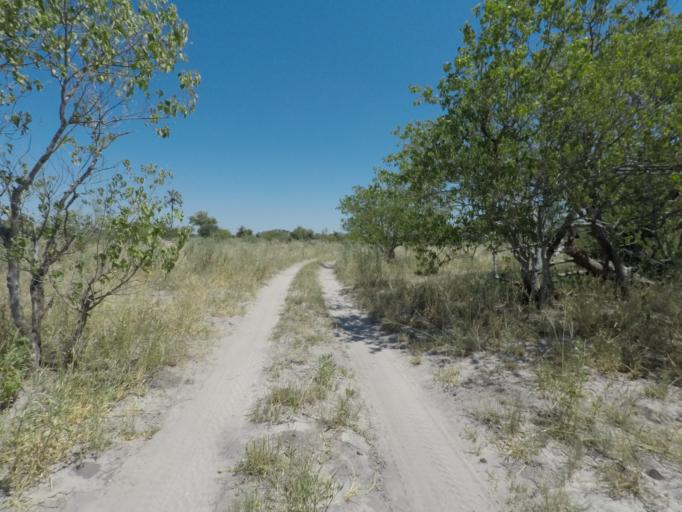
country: BW
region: North West
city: Maun
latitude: -19.4417
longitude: 23.5606
